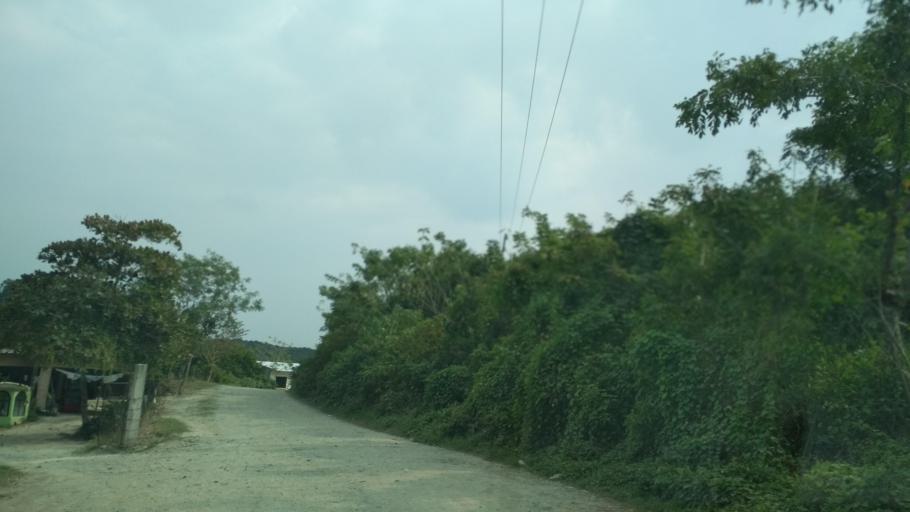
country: MM
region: Kayah
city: Loikaw
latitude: 20.2354
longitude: 97.2787
